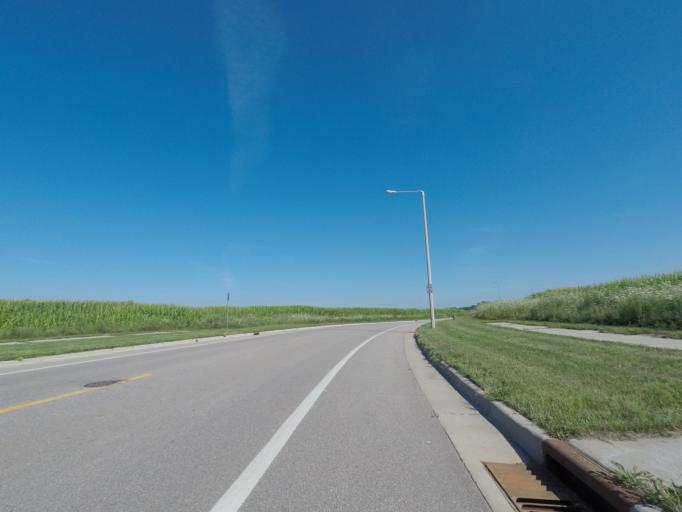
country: US
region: Wisconsin
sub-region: Dane County
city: Middleton
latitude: 43.0661
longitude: -89.5532
